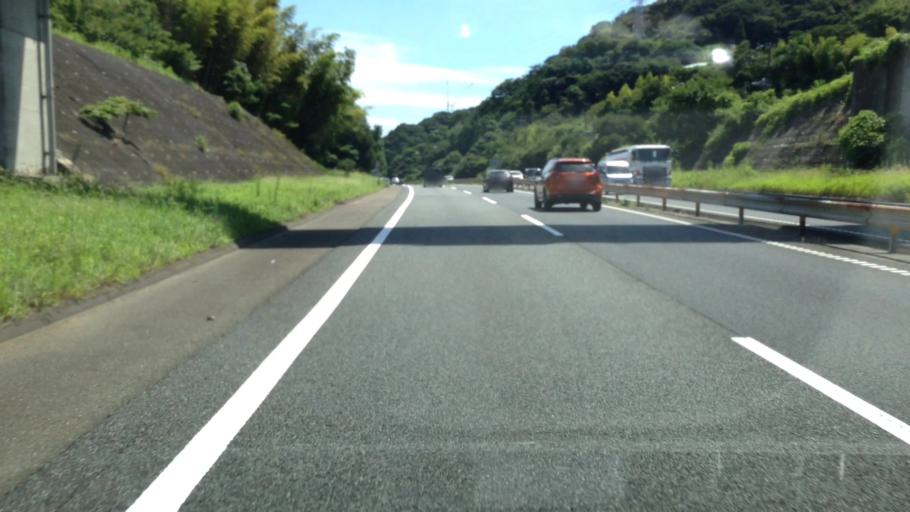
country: JP
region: Kanagawa
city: Yokosuka
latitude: 35.2590
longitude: 139.6343
